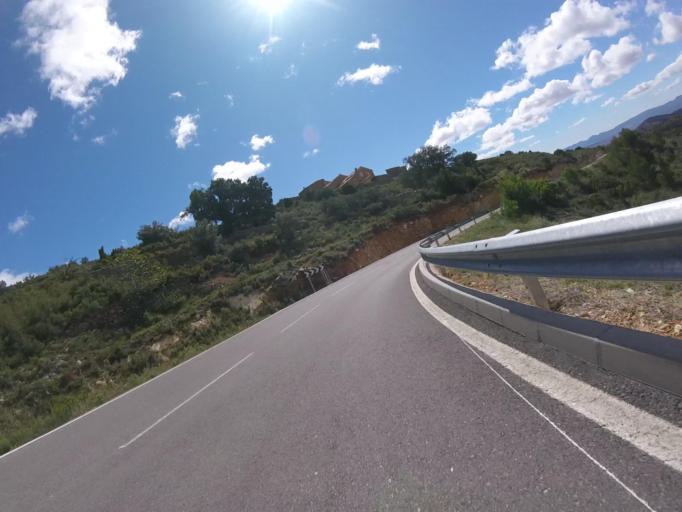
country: ES
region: Valencia
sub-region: Provincia de Castello
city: Culla
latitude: 40.3011
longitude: -0.1234
